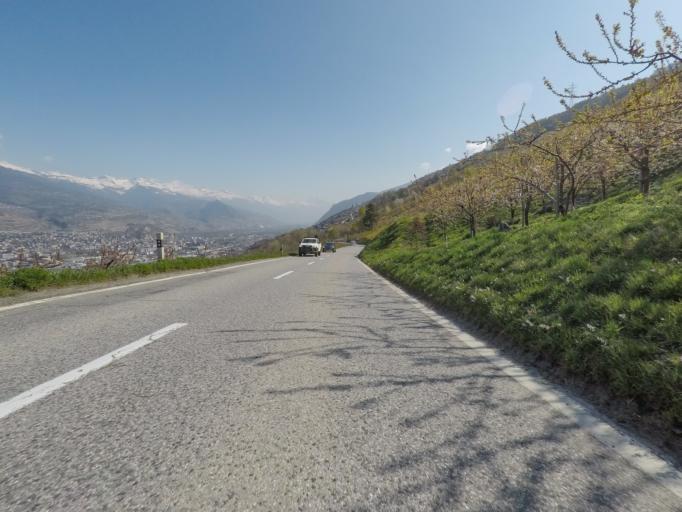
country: CH
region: Valais
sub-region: Conthey District
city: Basse-Nendaz
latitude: 46.2069
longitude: 7.3352
